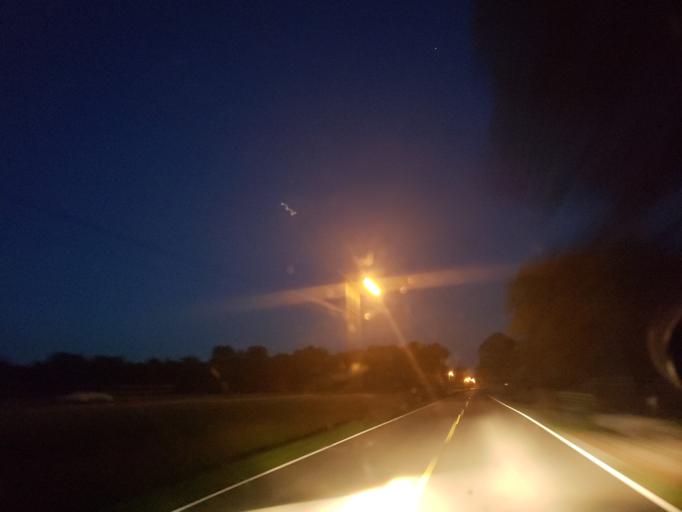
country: US
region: Alabama
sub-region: Madison County
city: Hazel Green
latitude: 34.9768
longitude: -86.6138
